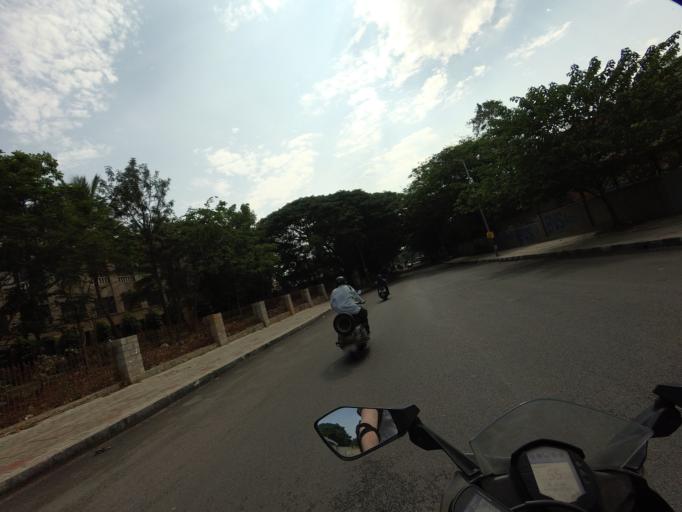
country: IN
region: Karnataka
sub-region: Bangalore Urban
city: Bangalore
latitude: 12.9750
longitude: 77.5850
